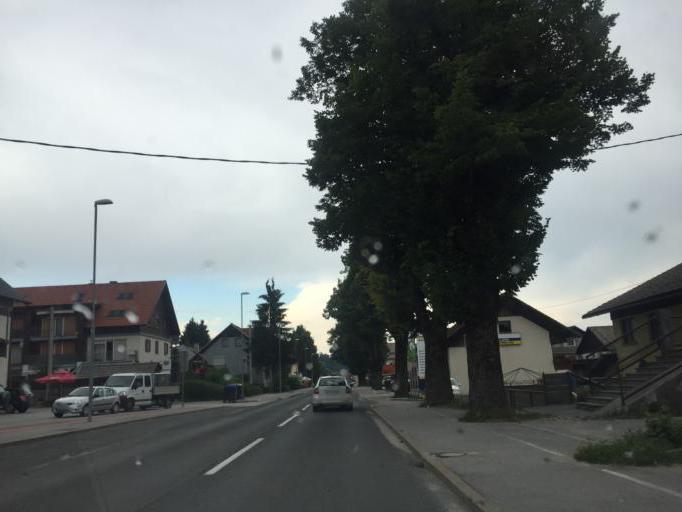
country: SI
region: Logatec
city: Logatec
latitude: 45.9118
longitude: 14.2057
